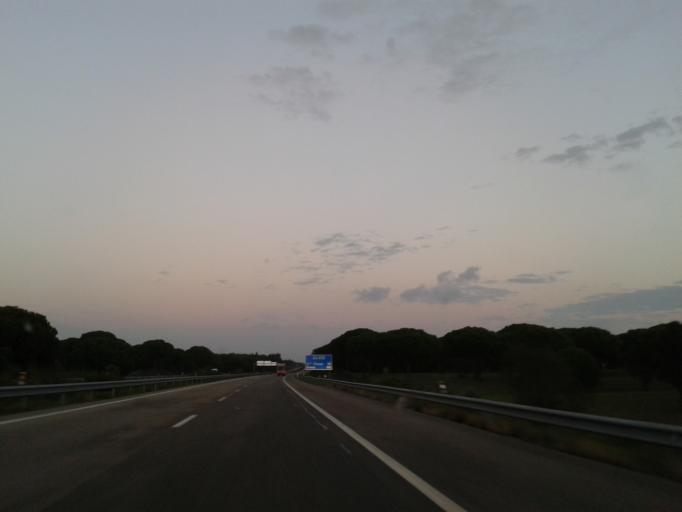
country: PT
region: Evora
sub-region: Vendas Novas
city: Vendas Novas
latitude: 38.6105
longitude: -8.6282
